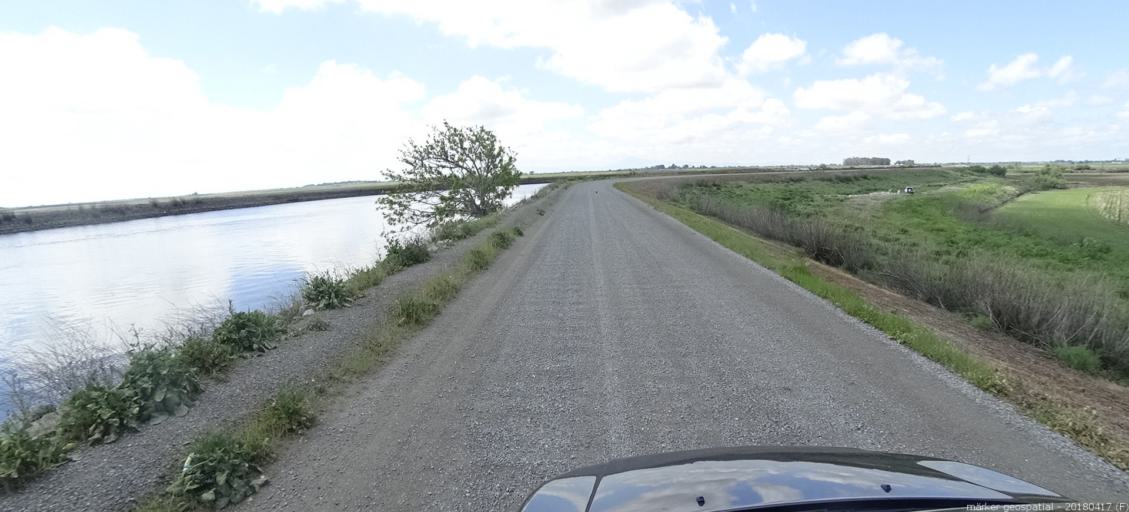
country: US
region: California
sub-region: Sacramento County
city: Walnut Grove
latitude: 38.1471
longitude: -121.5500
